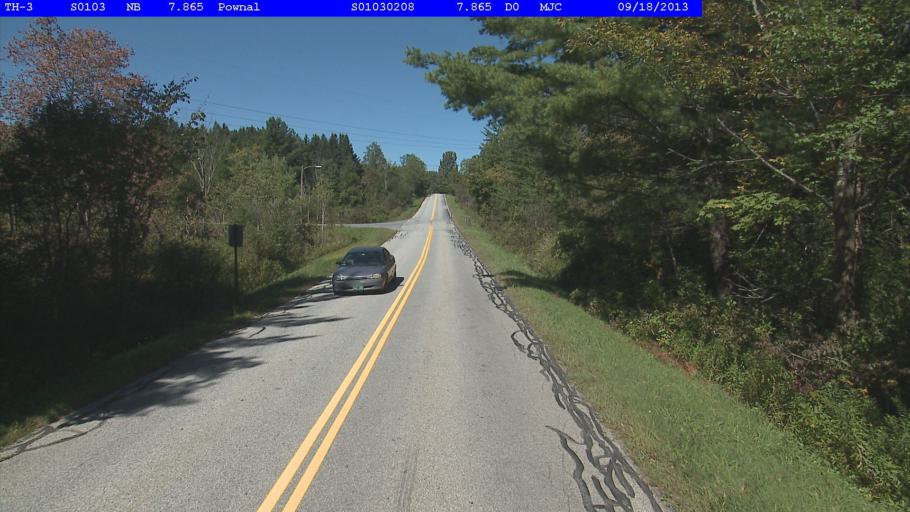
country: US
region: Vermont
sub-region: Bennington County
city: Bennington
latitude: 42.8334
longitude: -73.1682
